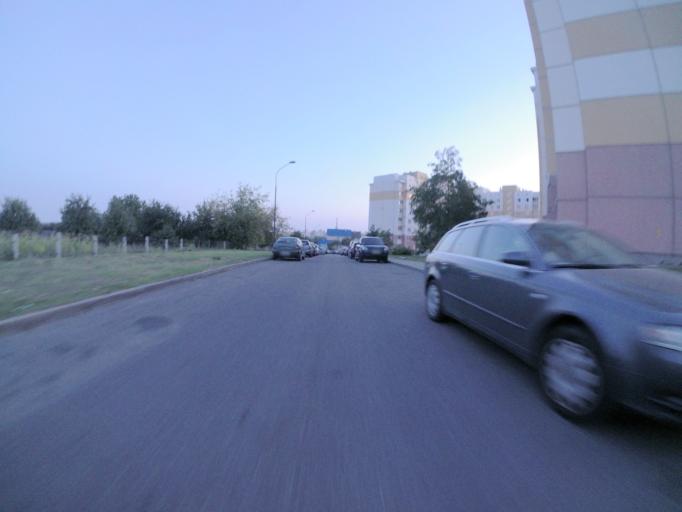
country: BY
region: Grodnenskaya
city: Hrodna
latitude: 53.7120
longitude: 23.8689
